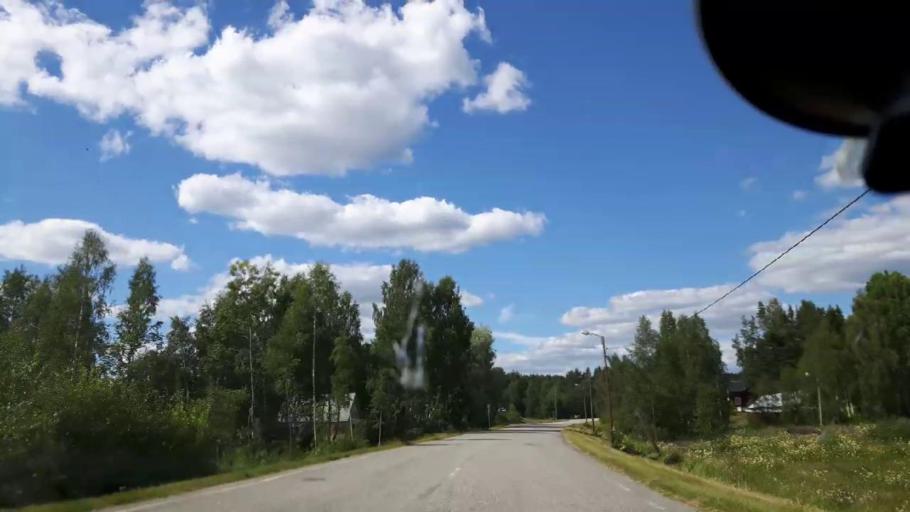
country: SE
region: Vaesternorrland
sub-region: Ange Kommun
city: Fransta
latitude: 62.7946
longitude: 16.2113
